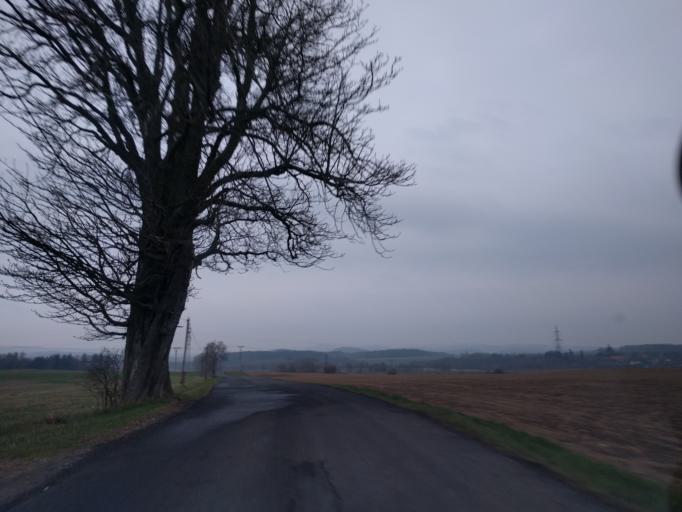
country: CZ
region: Karlovarsky
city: Bochov
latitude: 50.1378
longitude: 13.0885
